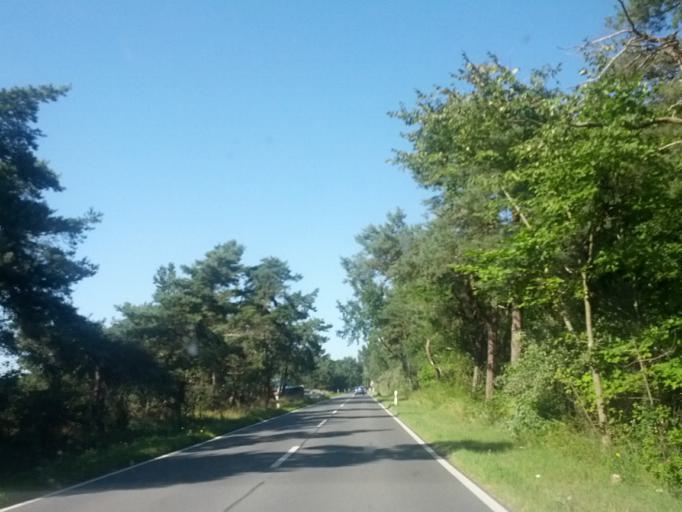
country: DE
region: Mecklenburg-Vorpommern
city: Ostseebad Gohren
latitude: 54.3081
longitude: 13.7157
